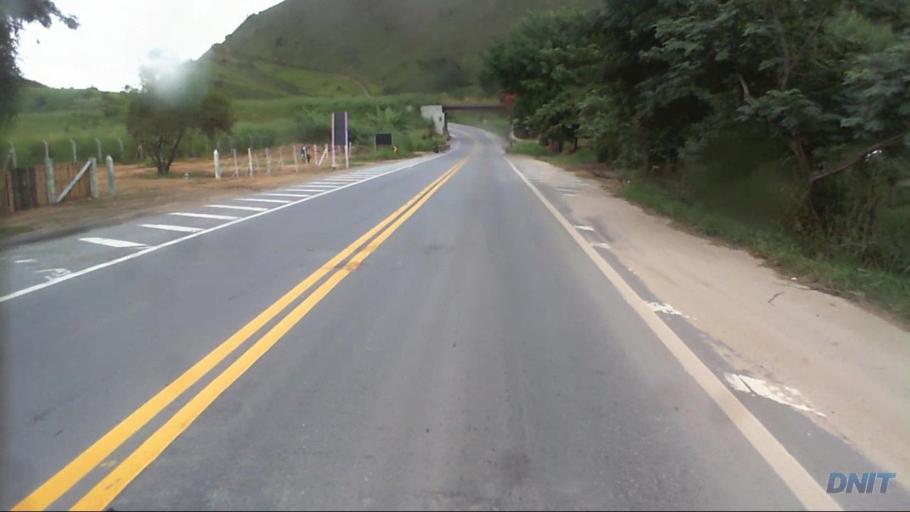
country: BR
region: Minas Gerais
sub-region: Nova Era
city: Nova Era
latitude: -19.7220
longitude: -43.0074
